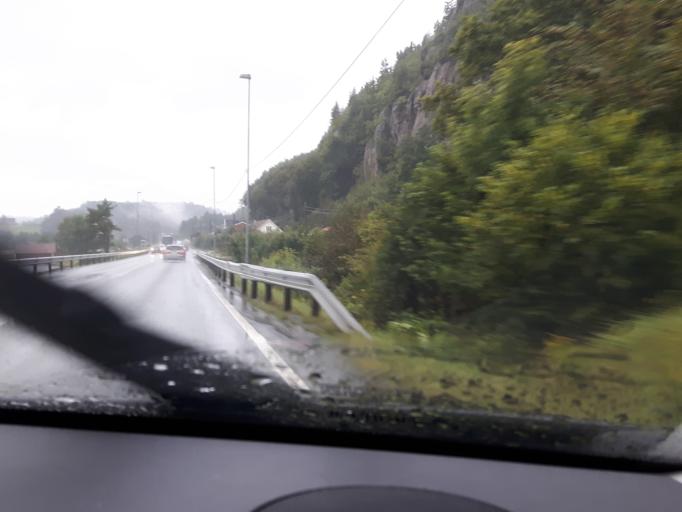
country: NO
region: Vest-Agder
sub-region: Mandal
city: Mandal
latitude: 58.0470
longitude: 7.4153
